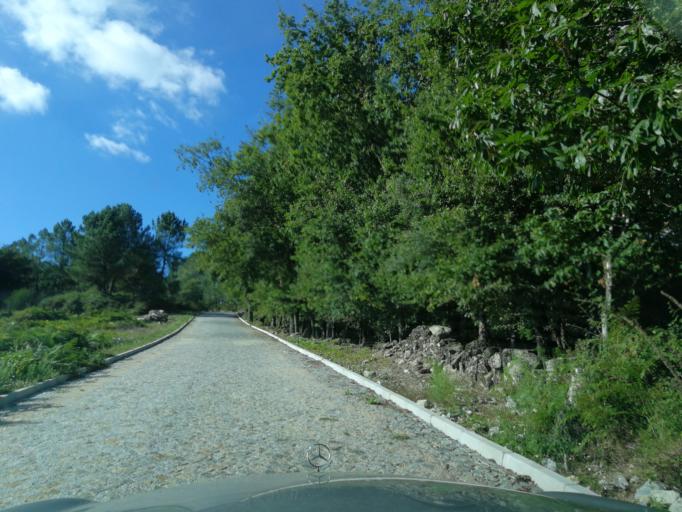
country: PT
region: Braga
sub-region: Braga
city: Adaufe
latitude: 41.5738
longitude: -8.3809
